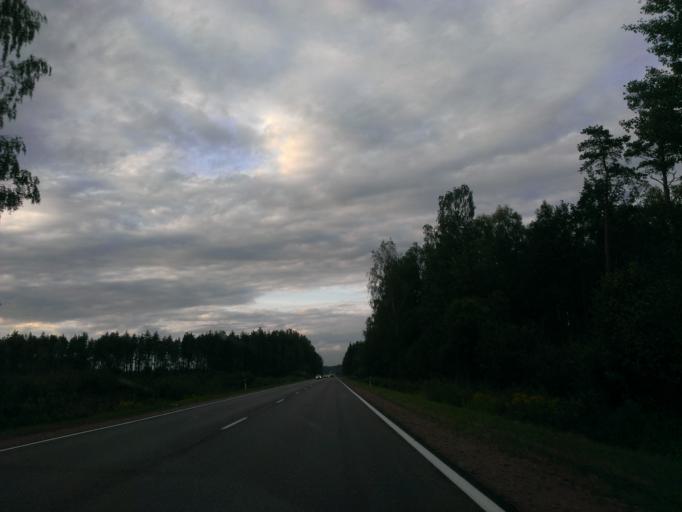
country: LV
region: Salaspils
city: Salaspils
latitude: 56.8875
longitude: 24.4075
